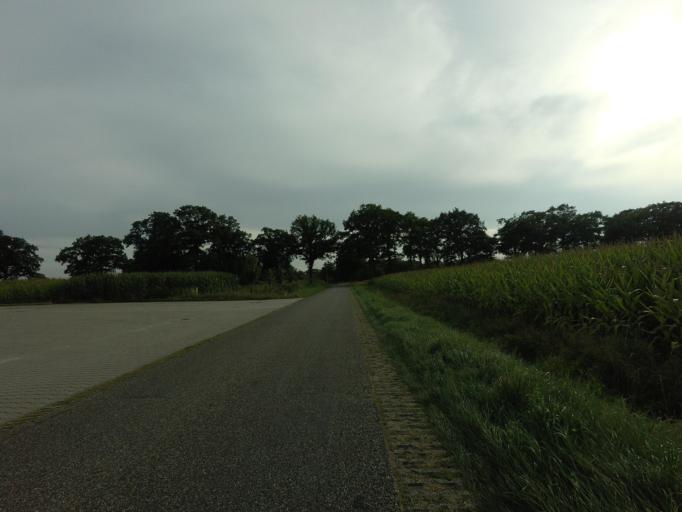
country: NL
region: Overijssel
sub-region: Gemeente Hardenberg
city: Hardenberg
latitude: 52.5942
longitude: 6.6747
